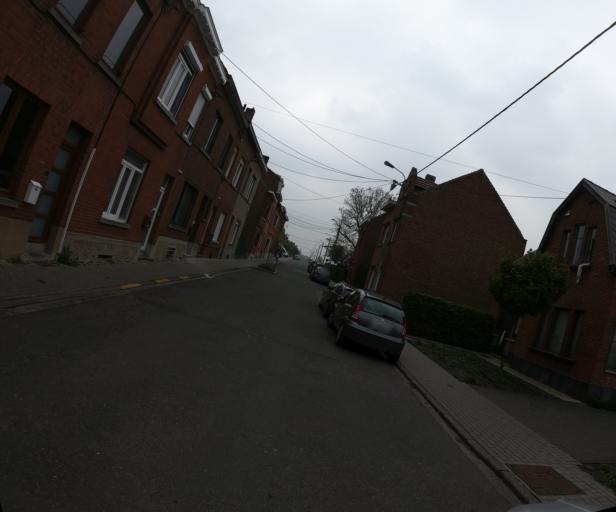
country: BE
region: Flanders
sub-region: Provincie Vlaams-Brabant
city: Halle
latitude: 50.7322
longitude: 4.2251
